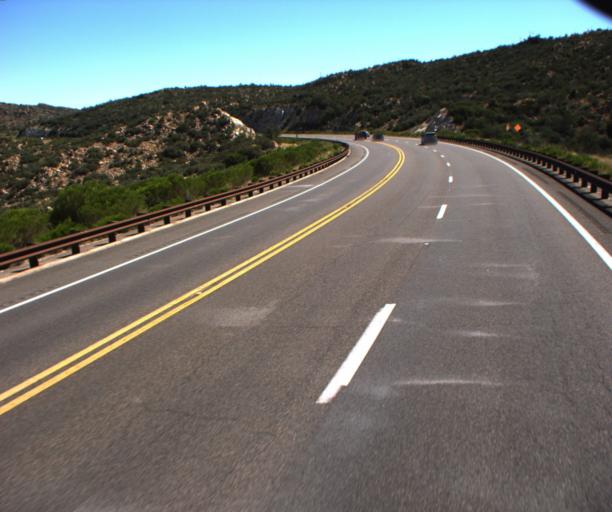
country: US
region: Arizona
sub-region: Gila County
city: Miami
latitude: 33.3613
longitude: -110.9448
